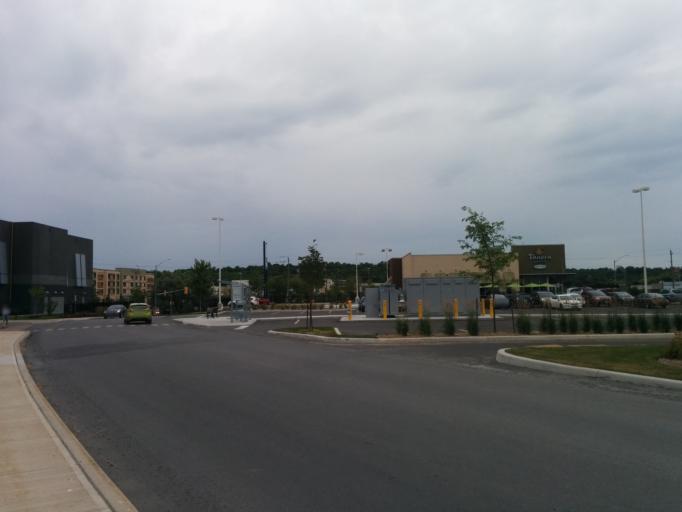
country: CA
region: Ontario
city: Kingston
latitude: 44.2646
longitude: -76.5026
